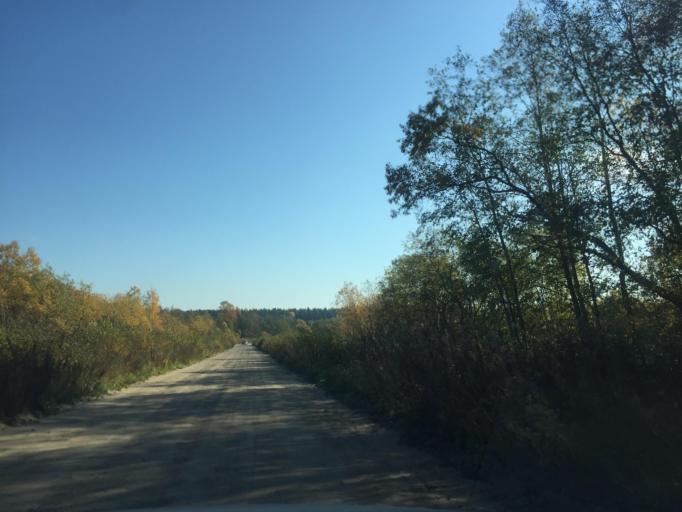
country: RU
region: Leningrad
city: Kuznechnoye
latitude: 61.2964
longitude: 30.0622
